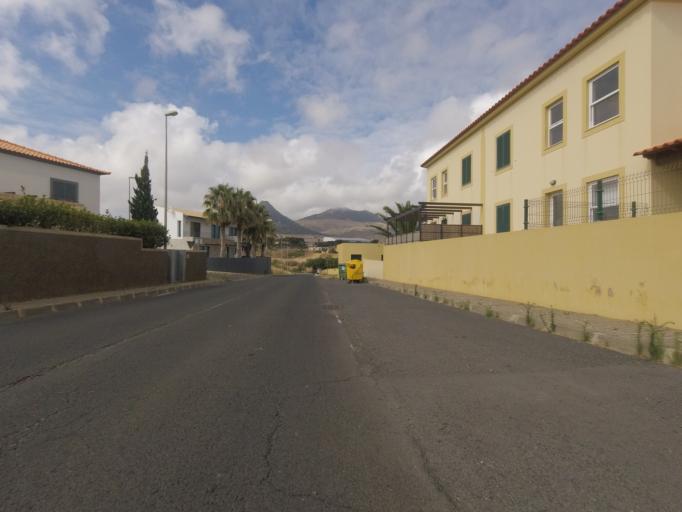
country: PT
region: Madeira
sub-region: Porto Santo
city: Vila de Porto Santo
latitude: 33.0567
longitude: -16.3416
